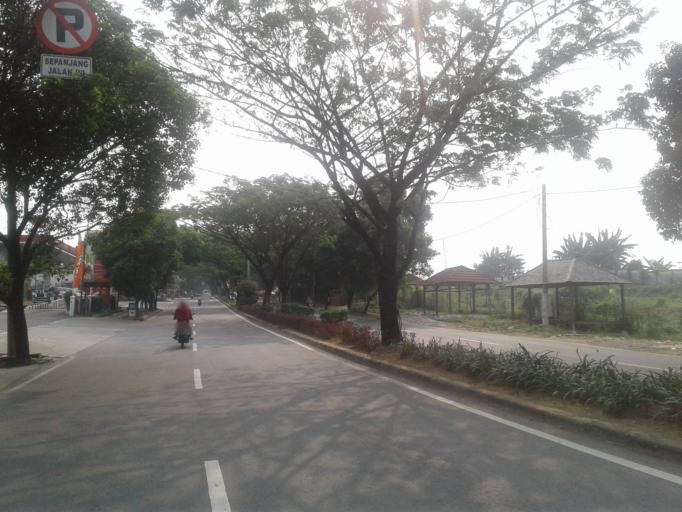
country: ID
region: West Java
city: Depok
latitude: -6.3809
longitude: 106.8569
